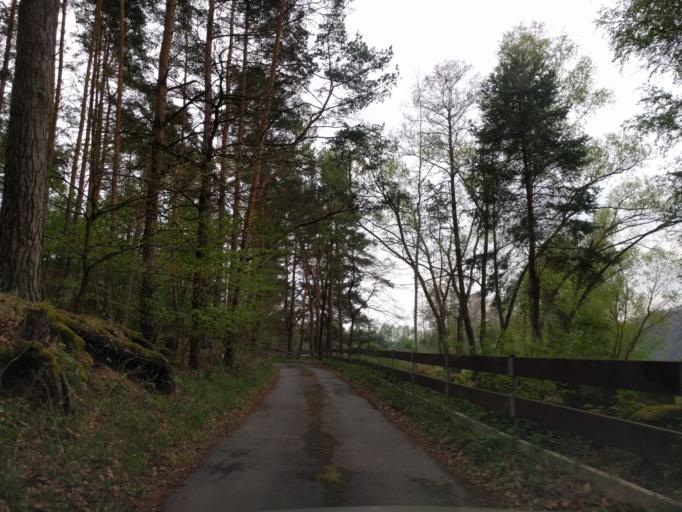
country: CZ
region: Central Bohemia
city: Krasna Hora nad Vltavou
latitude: 49.6694
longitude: 14.2621
